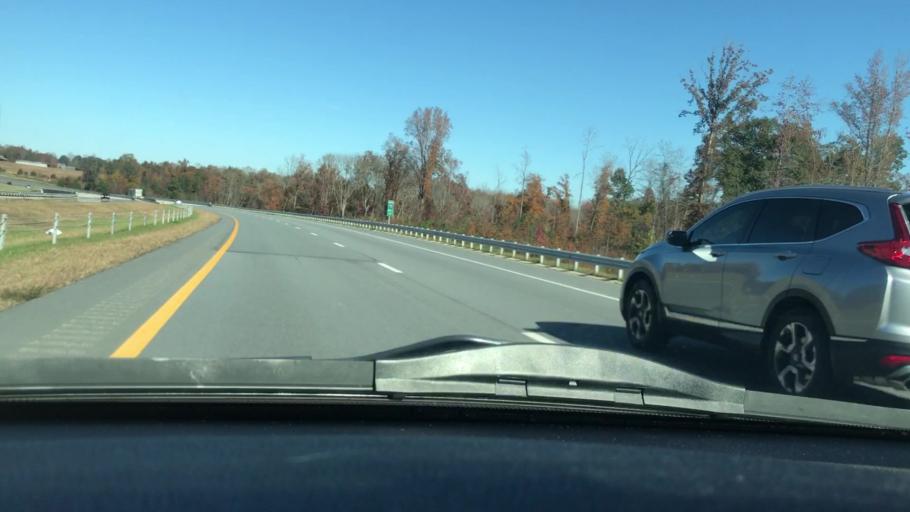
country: US
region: North Carolina
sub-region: Guilford County
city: Summerfield
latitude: 36.1756
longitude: -79.9368
